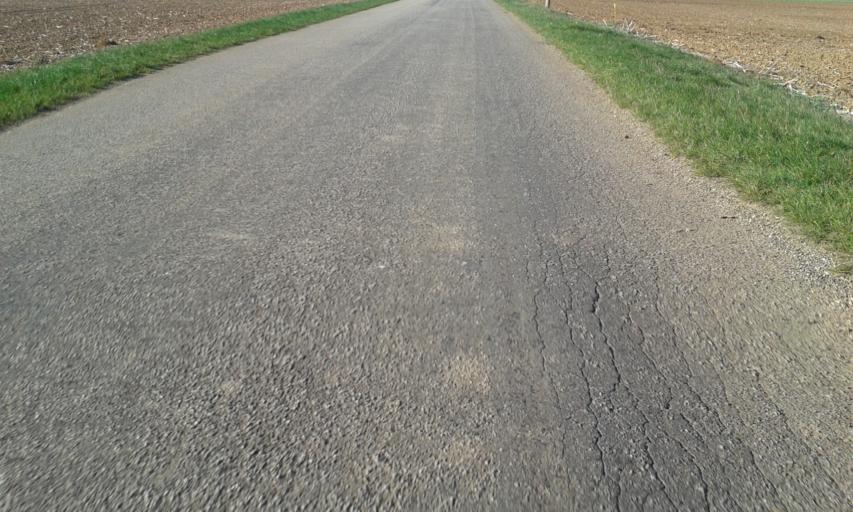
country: FR
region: Centre
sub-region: Departement du Loir-et-Cher
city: Mer
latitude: 47.7734
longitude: 1.4703
